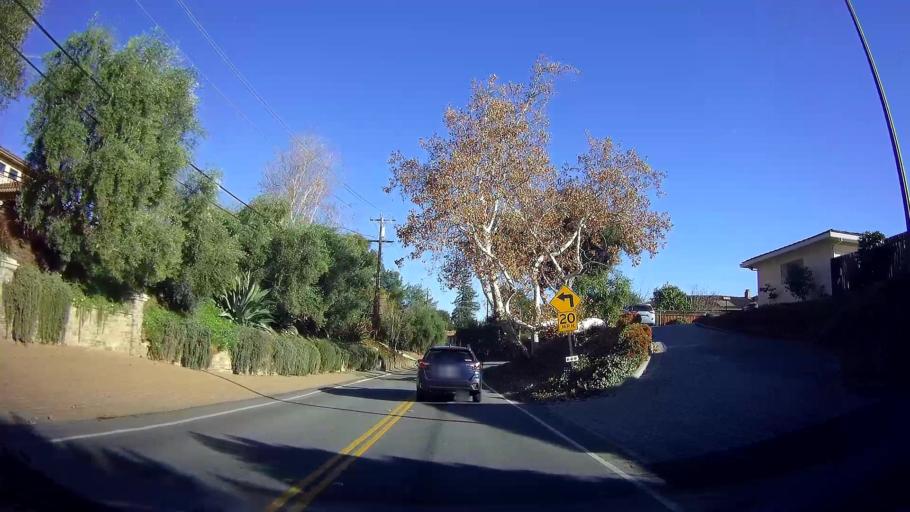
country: US
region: California
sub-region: Santa Clara County
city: Cambrian Park
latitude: 37.2806
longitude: -121.9250
